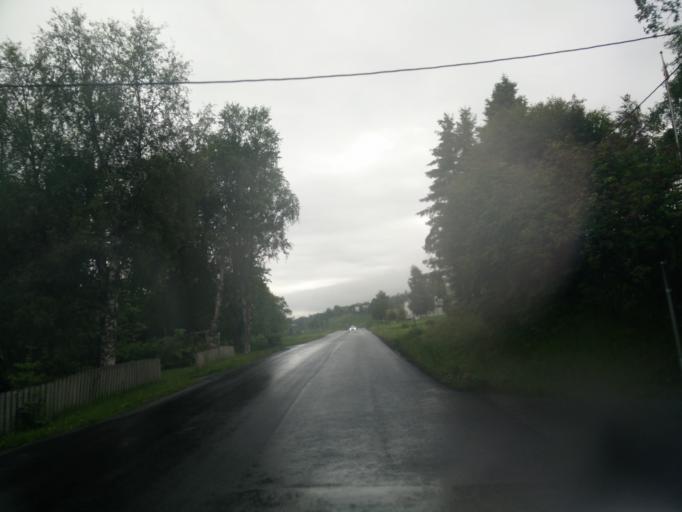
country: NO
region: Sor-Trondelag
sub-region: Orkdal
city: Orkanger
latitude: 63.2609
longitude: 9.7845
